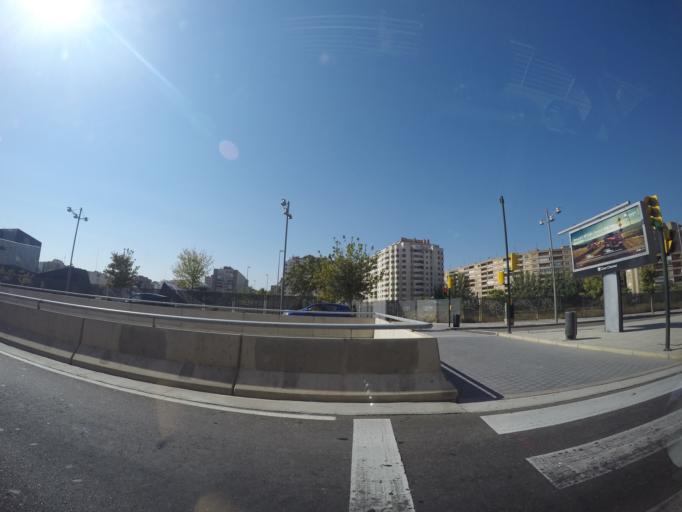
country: ES
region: Aragon
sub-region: Provincia de Zaragoza
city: Almozara
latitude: 41.6544
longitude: -0.8958
